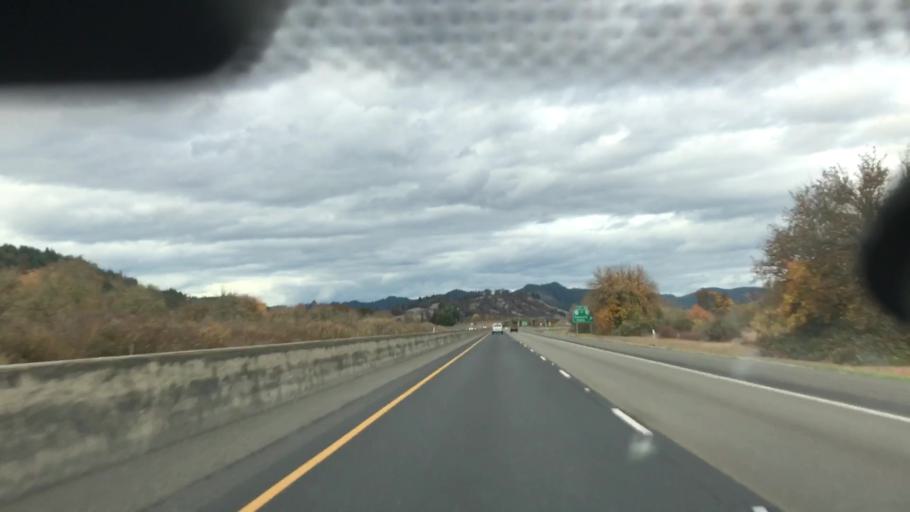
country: US
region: Oregon
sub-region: Douglas County
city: Yoncalla
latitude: 43.5567
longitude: -123.2834
